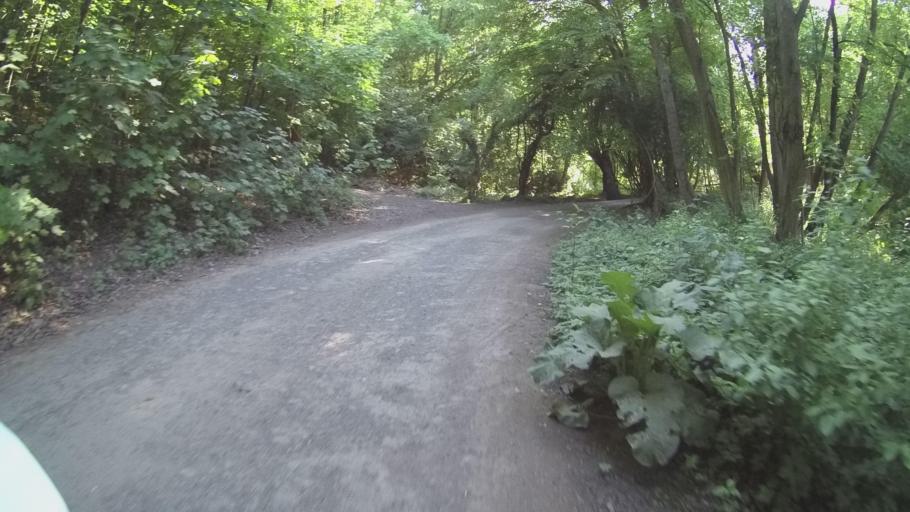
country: CZ
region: Central Bohemia
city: Roztoky
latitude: 50.1497
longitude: 14.4245
